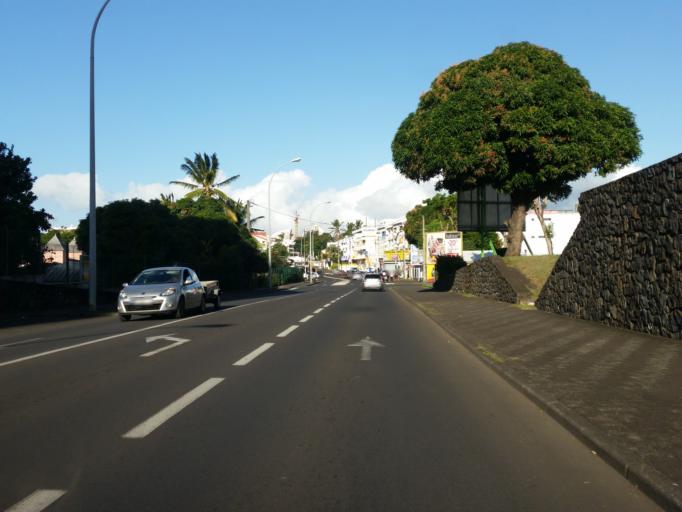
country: RE
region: Reunion
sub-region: Reunion
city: Saint-Denis
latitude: -20.8949
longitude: 55.4881
